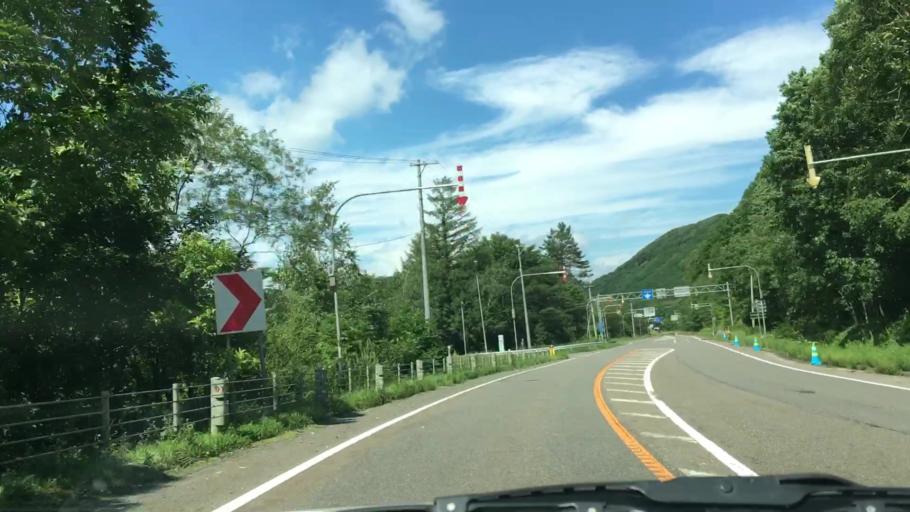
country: JP
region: Hokkaido
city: Otofuke
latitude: 43.2383
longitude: 143.4847
